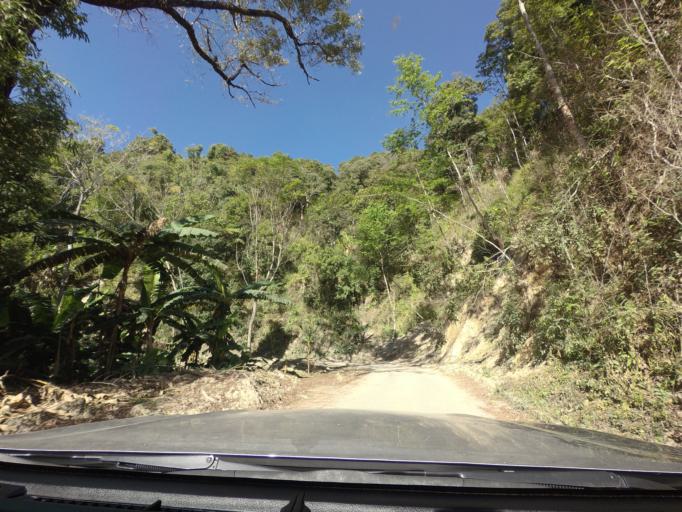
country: TH
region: Chiang Mai
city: Mae On
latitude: 18.8550
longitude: 99.3720
